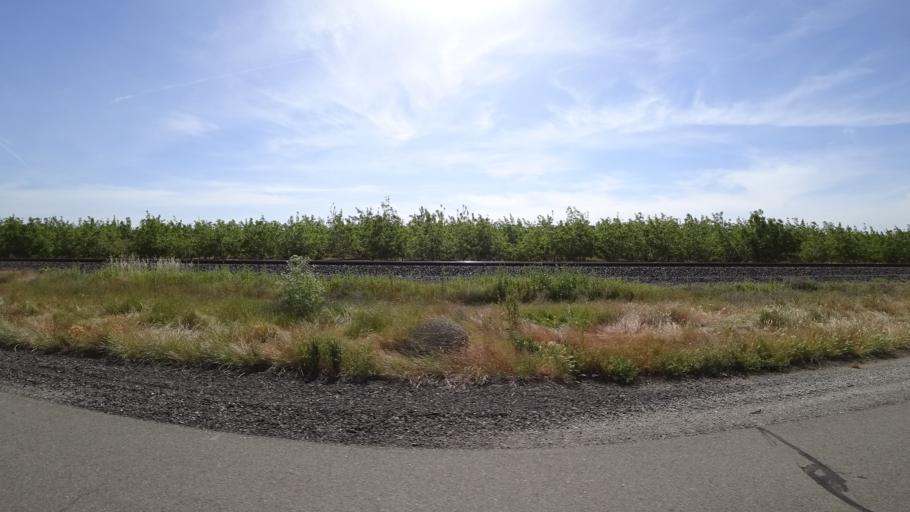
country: US
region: California
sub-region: Tehama County
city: Los Molinos
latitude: 39.9950
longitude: -122.0867
